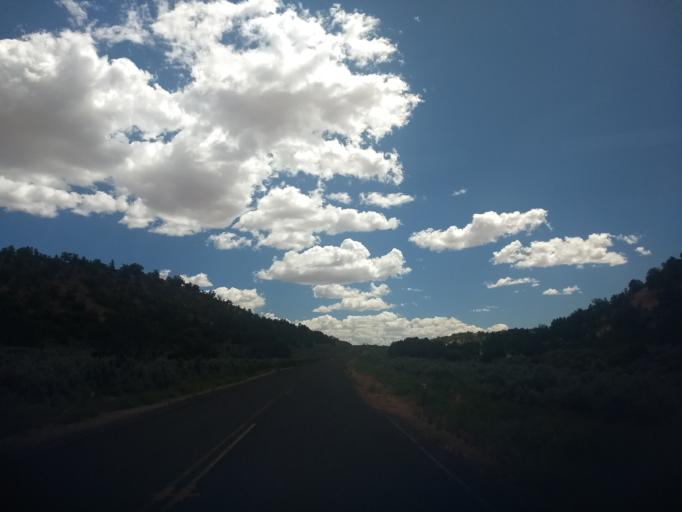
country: US
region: Utah
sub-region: Kane County
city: Kanab
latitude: 37.1119
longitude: -112.6782
